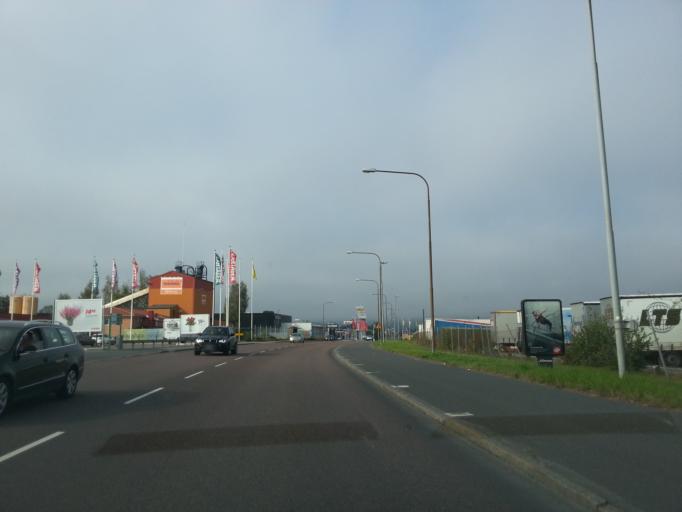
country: SE
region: Joenkoeping
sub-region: Jonkopings Kommun
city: Jonkoping
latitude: 57.7621
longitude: 14.1820
